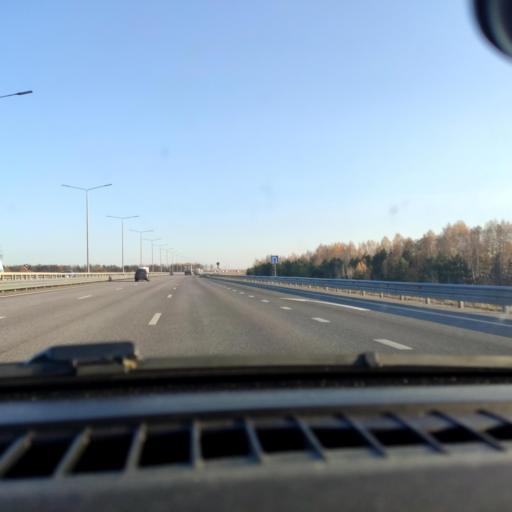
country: RU
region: Voronezj
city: Somovo
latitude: 51.7859
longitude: 39.2858
